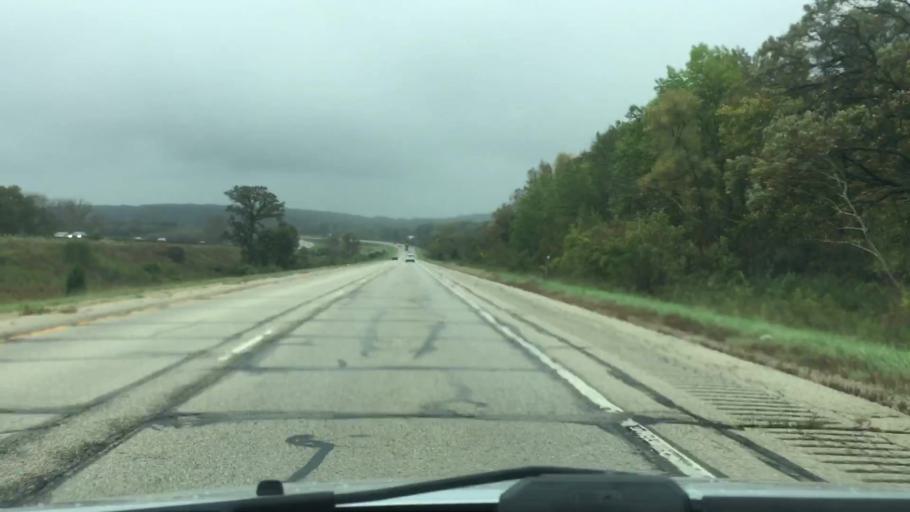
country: US
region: Wisconsin
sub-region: Walworth County
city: Como
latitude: 42.6241
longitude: -88.4658
